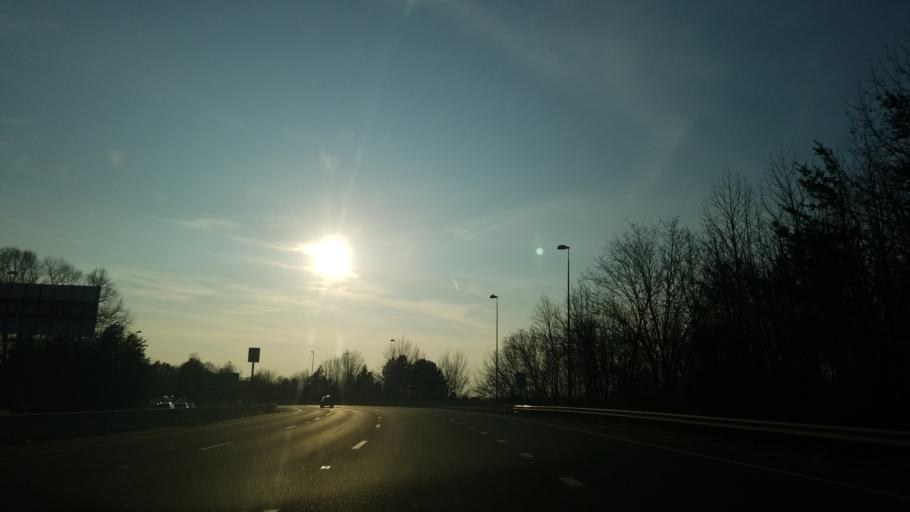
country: US
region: Virginia
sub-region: Fairfax County
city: Greenbriar
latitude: 38.8600
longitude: -77.3865
